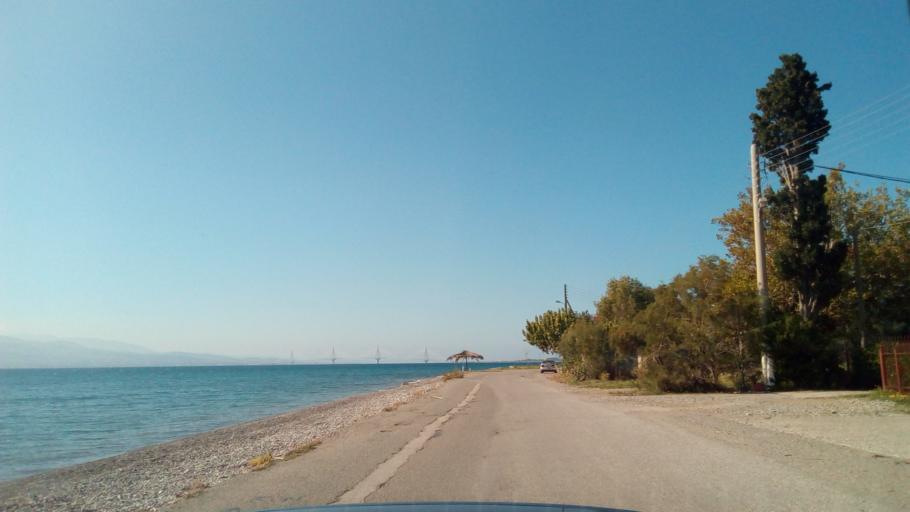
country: GR
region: West Greece
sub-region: Nomos Aitolias kai Akarnanias
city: Nafpaktos
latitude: 38.3809
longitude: 21.8128
